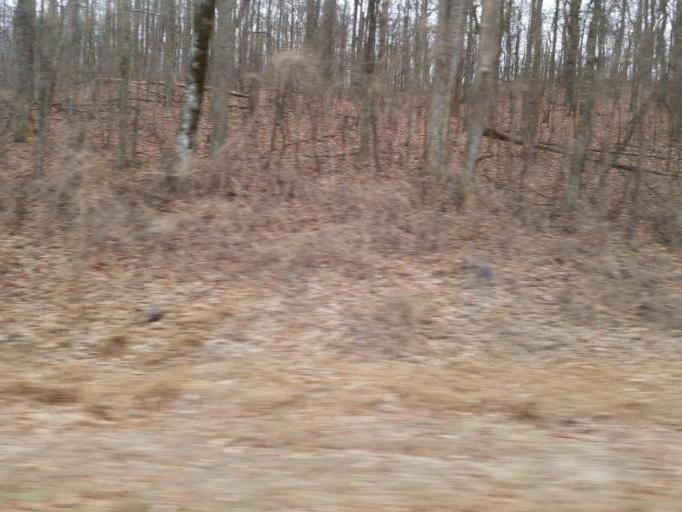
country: US
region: Georgia
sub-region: Pickens County
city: Jasper
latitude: 34.5374
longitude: -84.3739
